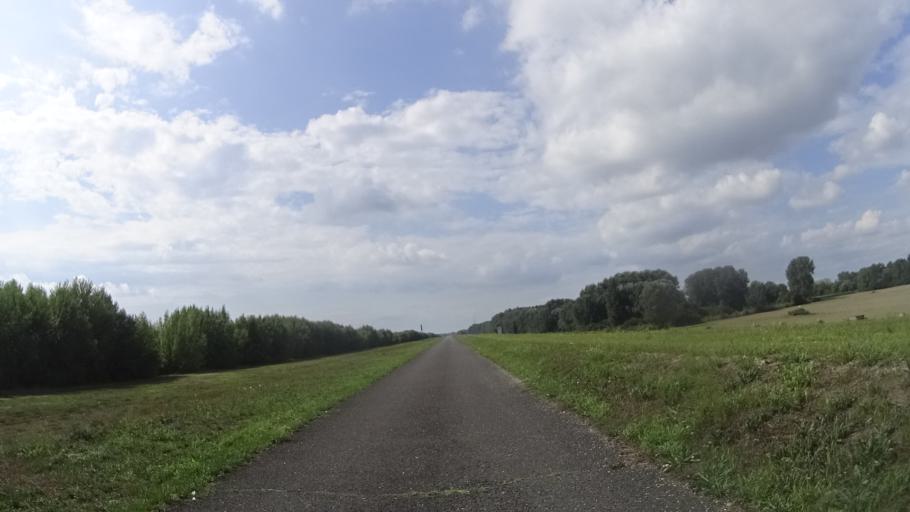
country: SK
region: Trnavsky
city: Gabcikovo
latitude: 47.8436
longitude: 17.5854
